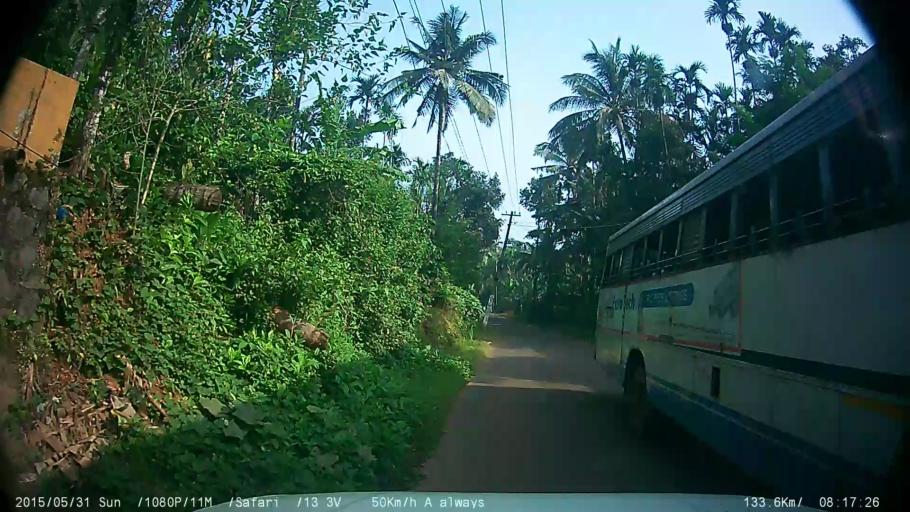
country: IN
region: Kerala
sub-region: Wayanad
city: Kalpetta
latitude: 11.6595
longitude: 75.9910
